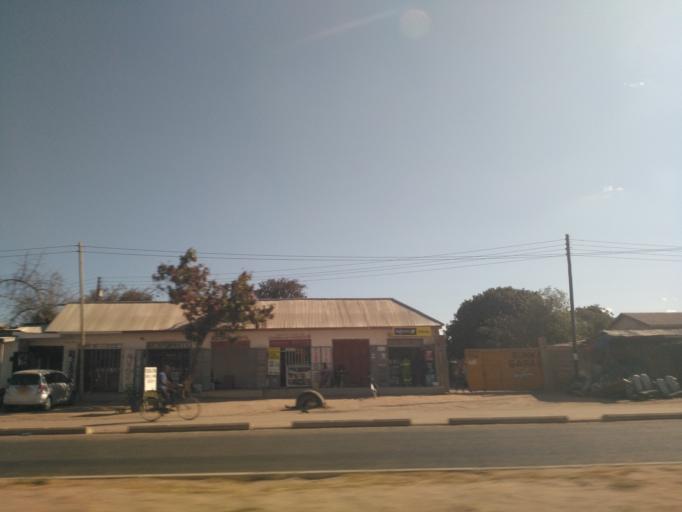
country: TZ
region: Dodoma
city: Dodoma
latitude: -6.1711
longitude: 35.7305
